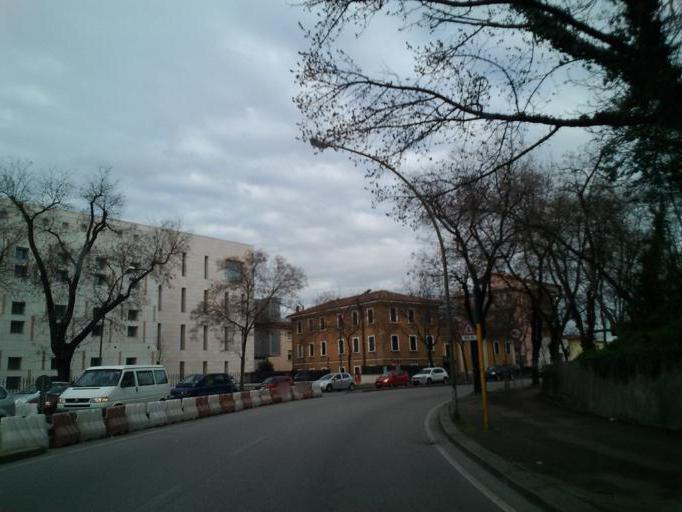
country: IT
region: Veneto
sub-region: Provincia di Verona
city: Verona
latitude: 45.4302
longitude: 10.9945
